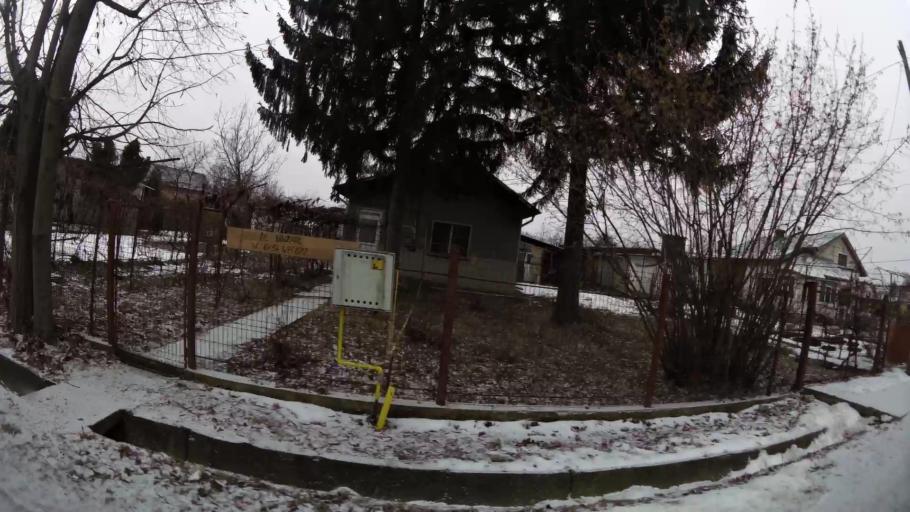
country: RO
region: Dambovita
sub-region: Municipiul Targoviste
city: Targoviste
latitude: 44.9418
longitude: 25.4748
